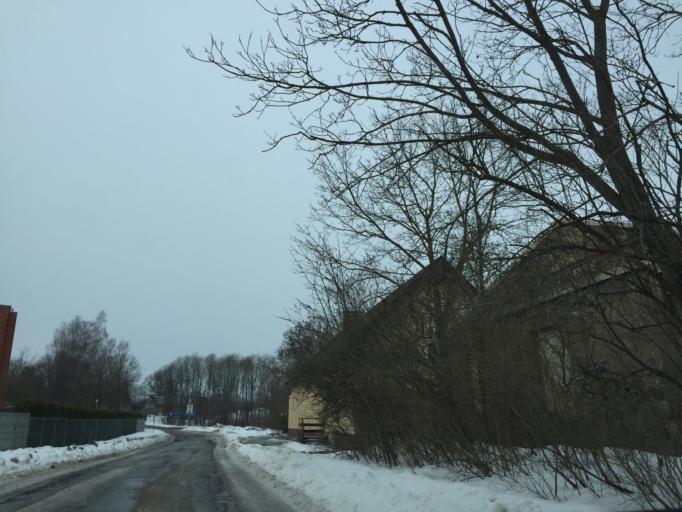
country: LV
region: Ikskile
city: Ikskile
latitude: 56.8453
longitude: 24.4435
